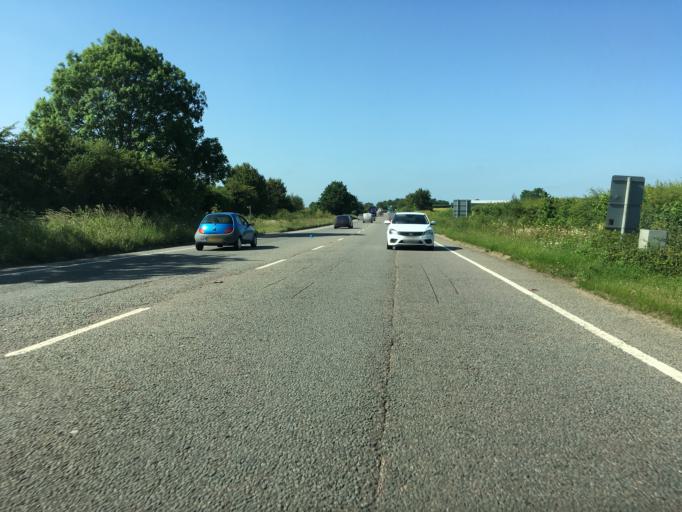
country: GB
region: England
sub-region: Milton Keynes
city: Water Eaton
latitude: 51.9857
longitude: -0.7015
